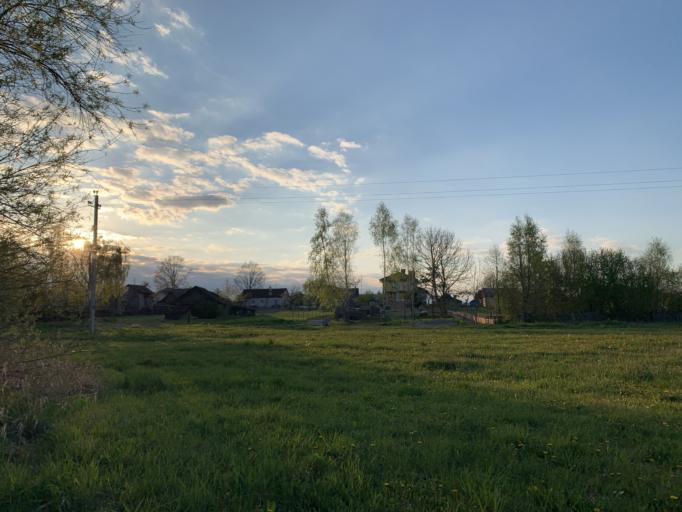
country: BY
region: Minsk
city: Nyasvizh
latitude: 53.2316
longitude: 26.6924
